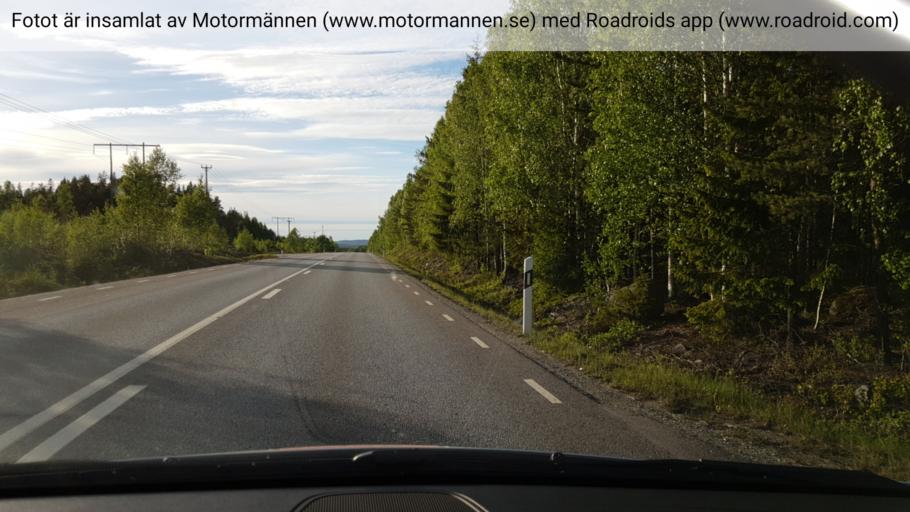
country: SE
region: Vaestmanland
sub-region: Skinnskattebergs Kommun
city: Skinnskatteberg
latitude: 59.8501
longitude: 15.6651
